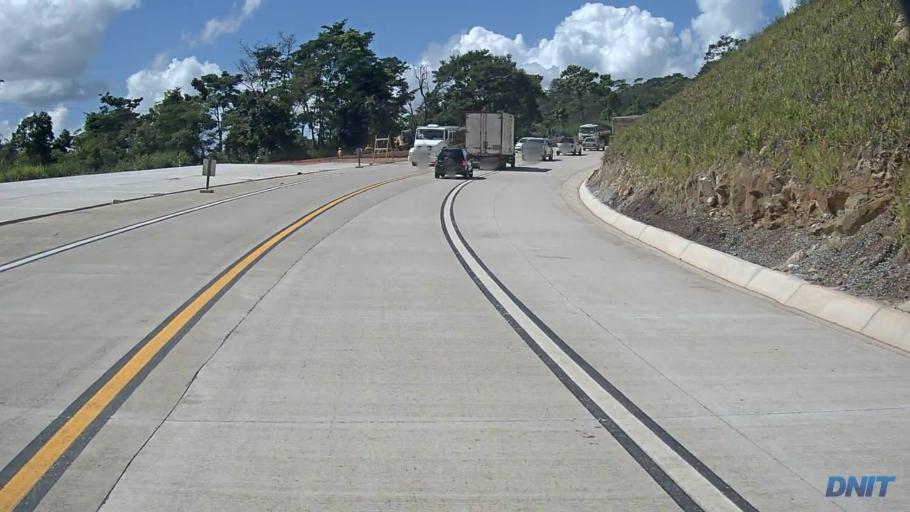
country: BR
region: Minas Gerais
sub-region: Caete
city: Caete
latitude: -19.7784
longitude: -43.6563
